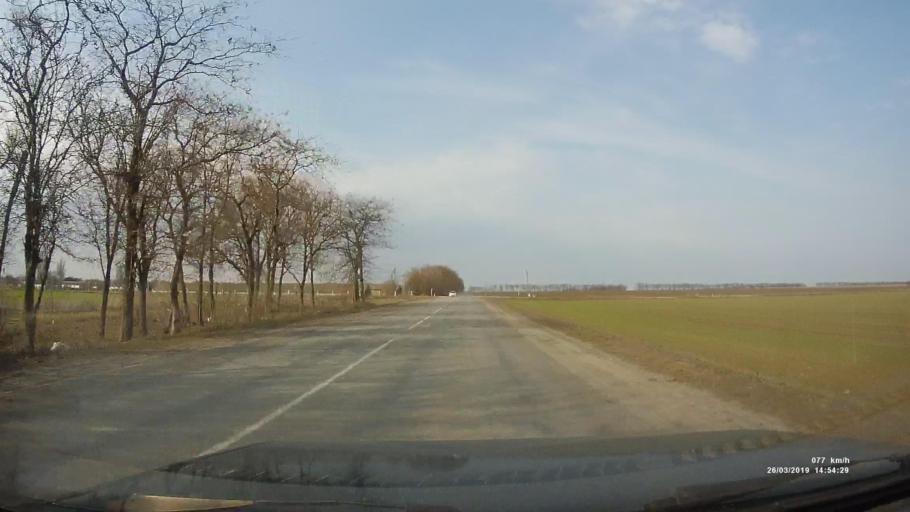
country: RU
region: Rostov
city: Novobessergenovka
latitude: 47.1942
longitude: 38.8132
